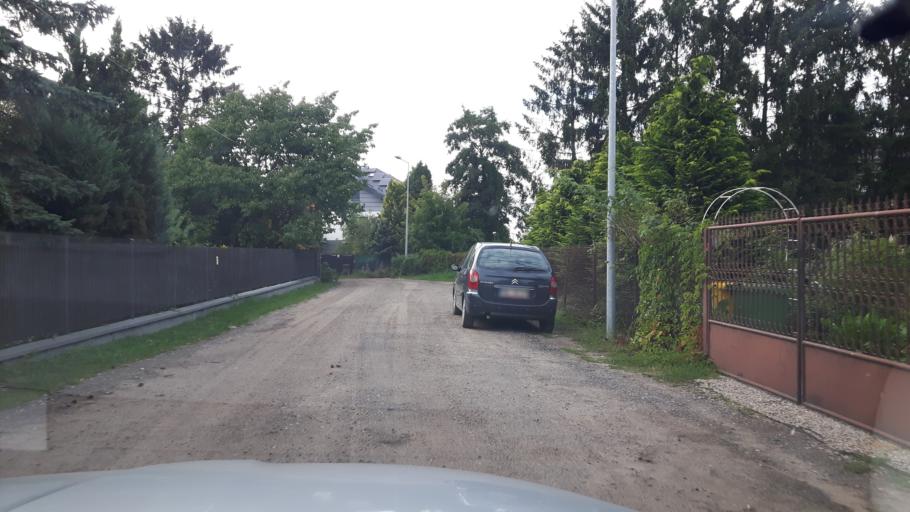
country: PL
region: Masovian Voivodeship
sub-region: Powiat wolominski
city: Marki
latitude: 52.3119
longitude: 21.0921
